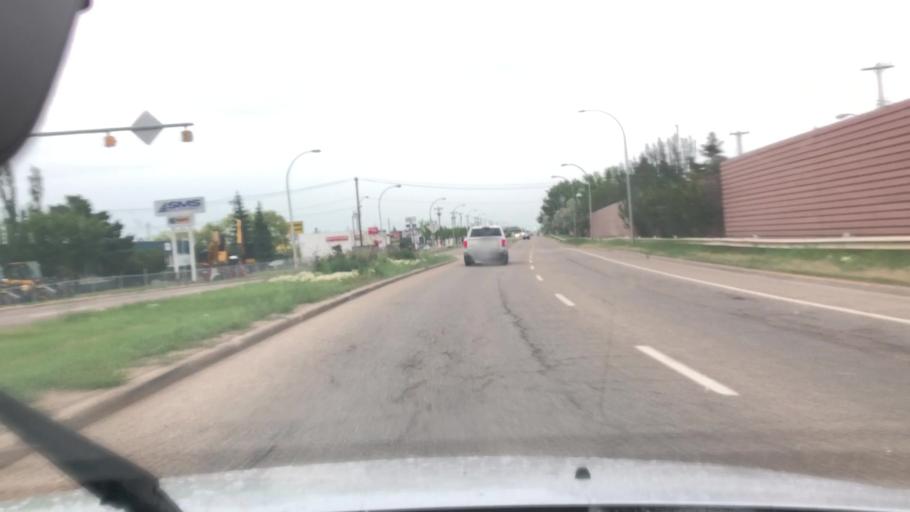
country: CA
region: Alberta
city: St. Albert
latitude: 53.5589
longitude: -113.6007
